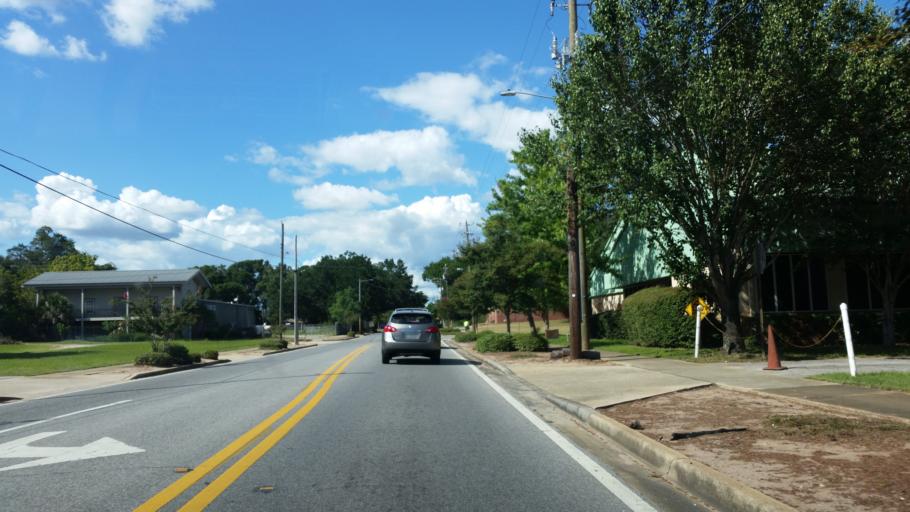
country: US
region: Florida
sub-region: Escambia County
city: Goulding
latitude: 30.4417
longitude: -87.2288
